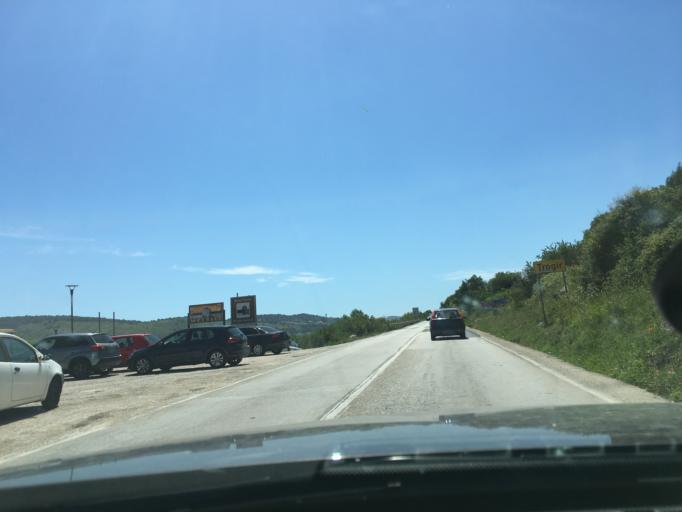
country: HR
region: Splitsko-Dalmatinska
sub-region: Grad Trogir
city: Trogir
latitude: 43.5303
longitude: 16.2771
